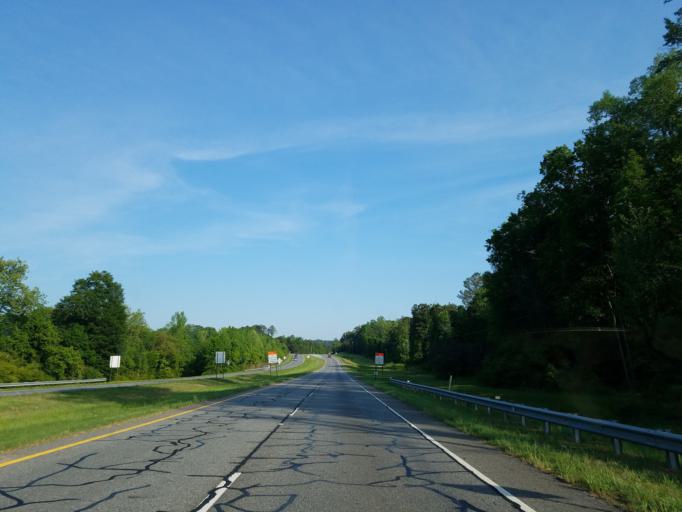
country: US
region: Georgia
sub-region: Chattooga County
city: Summerville
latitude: 34.4570
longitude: -85.2556
